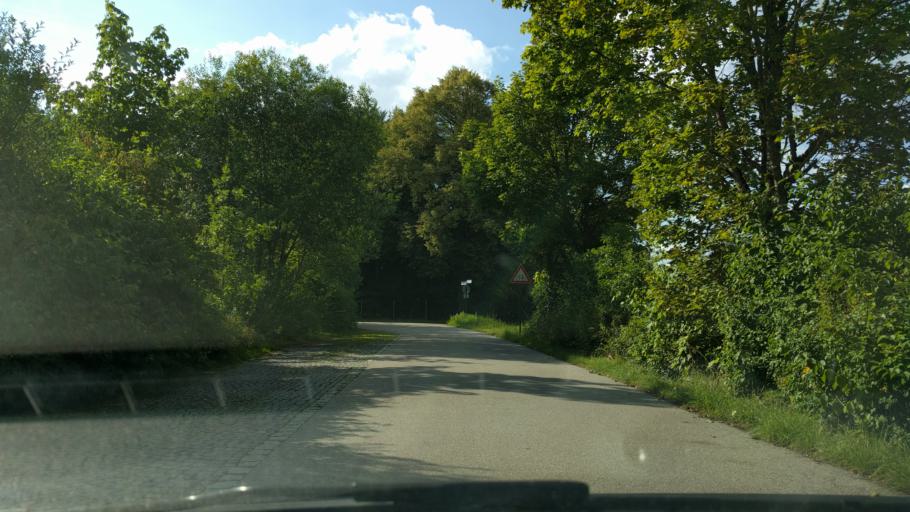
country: DE
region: Bavaria
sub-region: Upper Bavaria
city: Oberhaching
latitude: 48.0358
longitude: 11.5794
